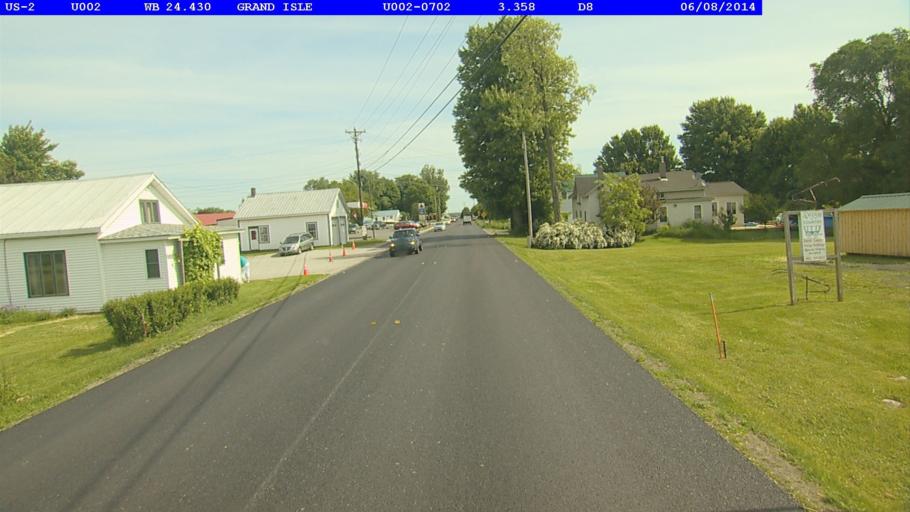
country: US
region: Vermont
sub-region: Grand Isle County
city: North Hero
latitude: 44.7194
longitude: -73.2949
